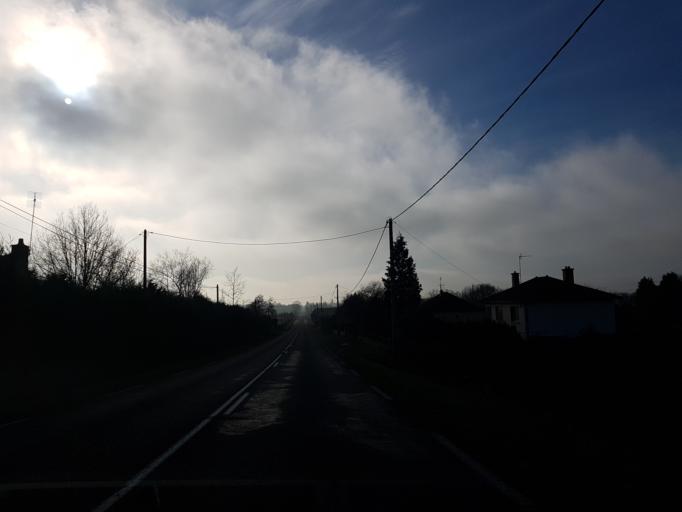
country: FR
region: Bourgogne
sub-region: Departement de Saone-et-Loire
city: Gueugnon
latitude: 46.6200
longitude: 4.0818
